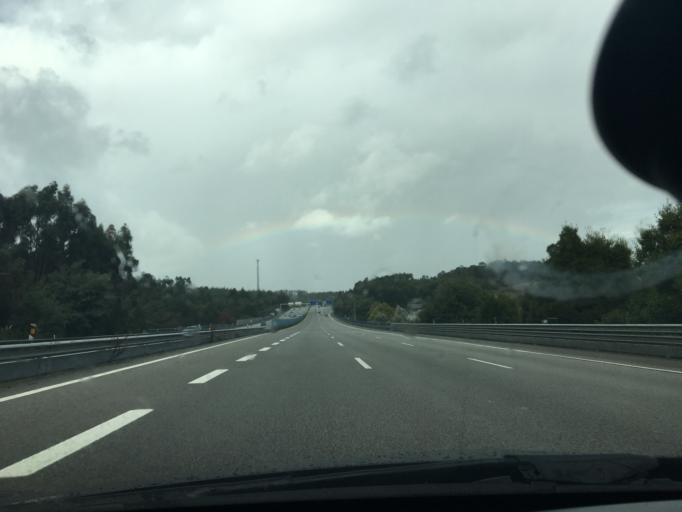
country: PT
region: Porto
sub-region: Matosinhos
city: Guifoes
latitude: 41.2166
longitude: -8.6560
